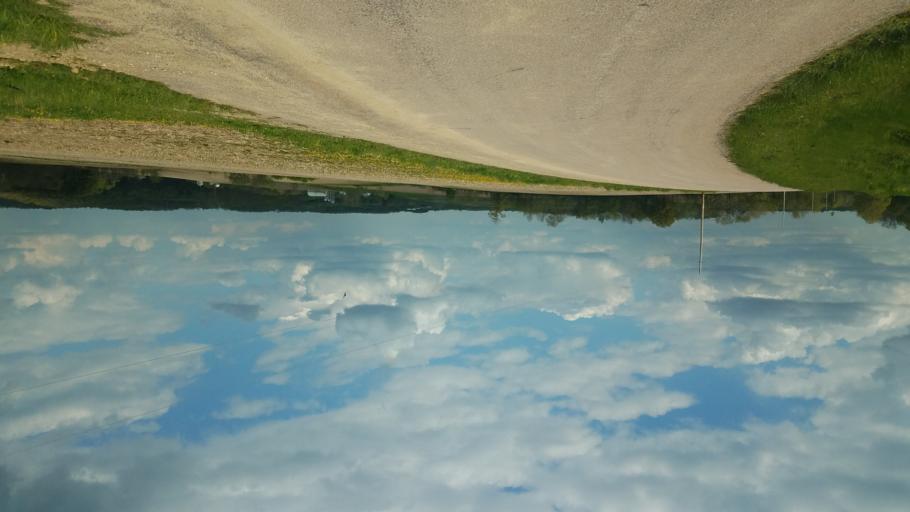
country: US
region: Wisconsin
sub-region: Vernon County
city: Hillsboro
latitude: 43.5759
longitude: -90.3316
